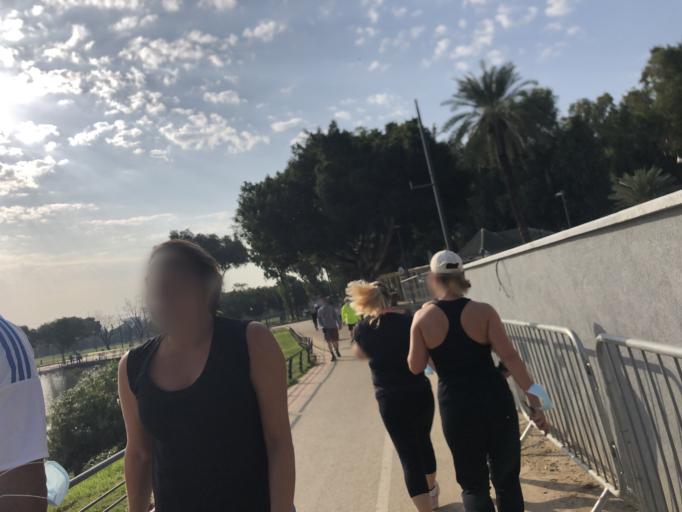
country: IL
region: Tel Aviv
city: Giv`atayim
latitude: 32.0499
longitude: 34.8232
